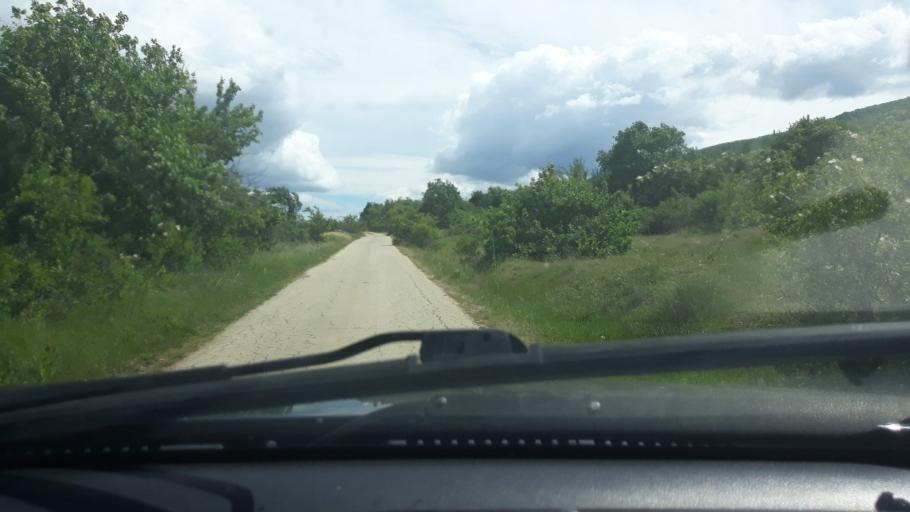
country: MK
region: Krivogastani
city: Krivogashtani
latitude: 41.3305
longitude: 21.3024
